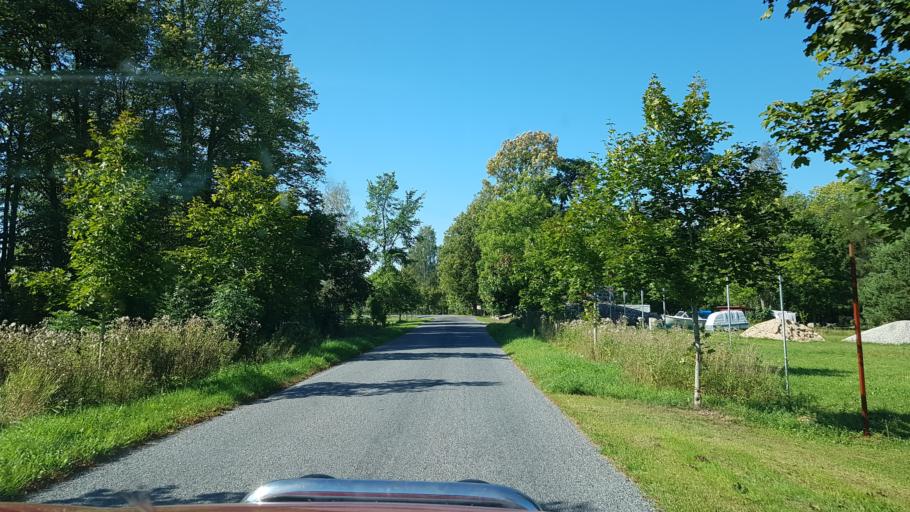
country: EE
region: Tartu
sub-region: UElenurme vald
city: Ulenurme
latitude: 58.3482
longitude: 26.8930
